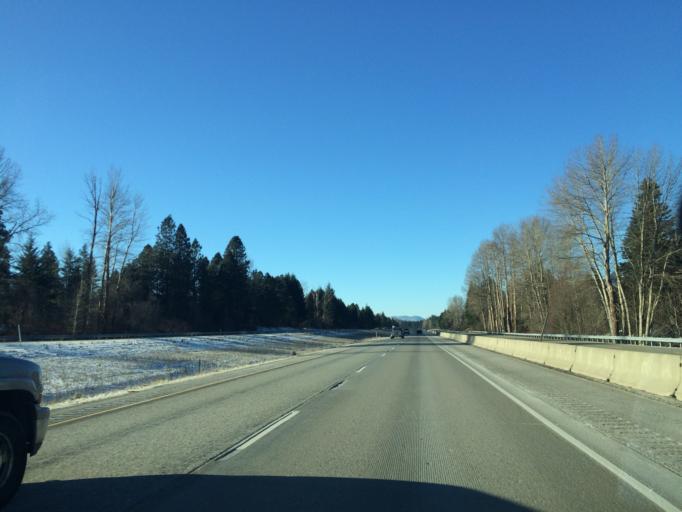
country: US
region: Washington
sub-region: Kittitas County
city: Cle Elum
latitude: 47.2061
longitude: -121.0856
